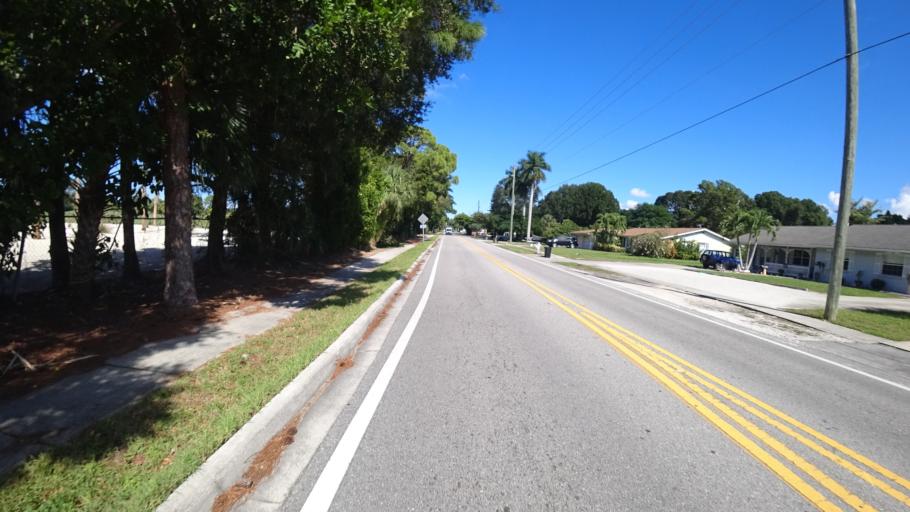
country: US
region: Florida
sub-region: Manatee County
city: West Bradenton
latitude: 27.4855
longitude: -82.6040
